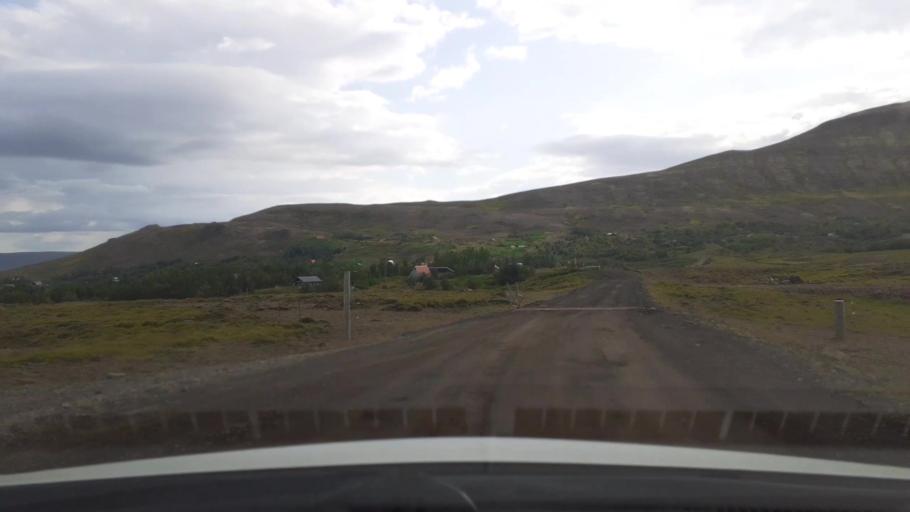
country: IS
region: Capital Region
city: Mosfellsbaer
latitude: 64.2963
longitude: -21.6557
